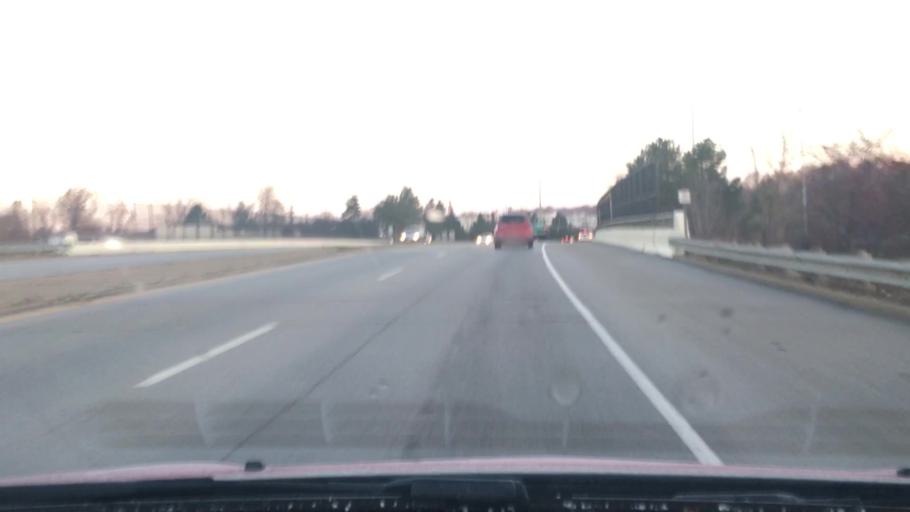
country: US
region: Ohio
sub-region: Wayne County
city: Wooster
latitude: 40.7896
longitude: -81.9351
